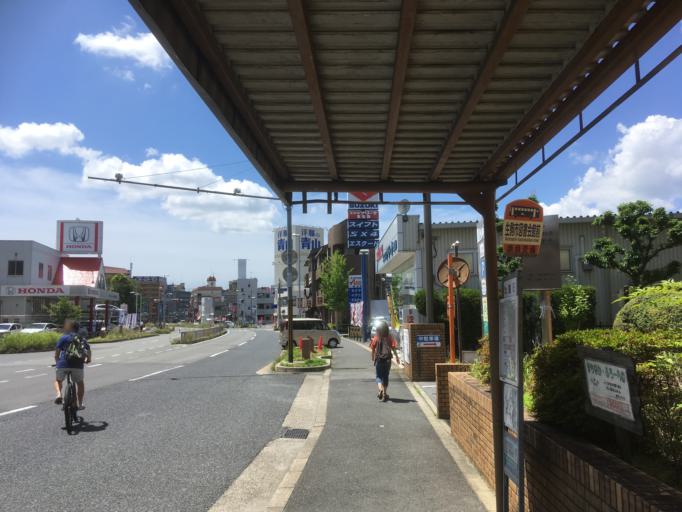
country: JP
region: Nara
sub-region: Ikoma-shi
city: Ikoma
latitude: 34.6963
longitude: 135.7088
